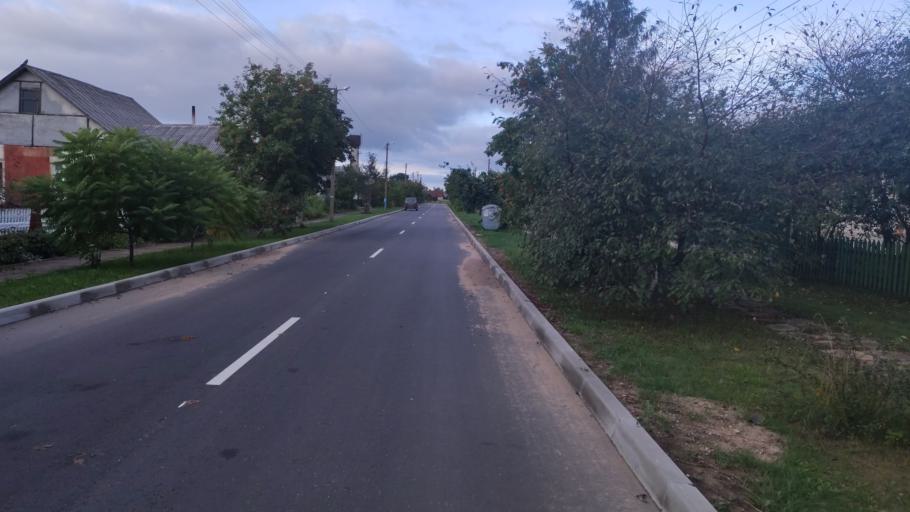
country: BY
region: Minsk
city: Narach
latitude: 54.9325
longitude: 26.6917
